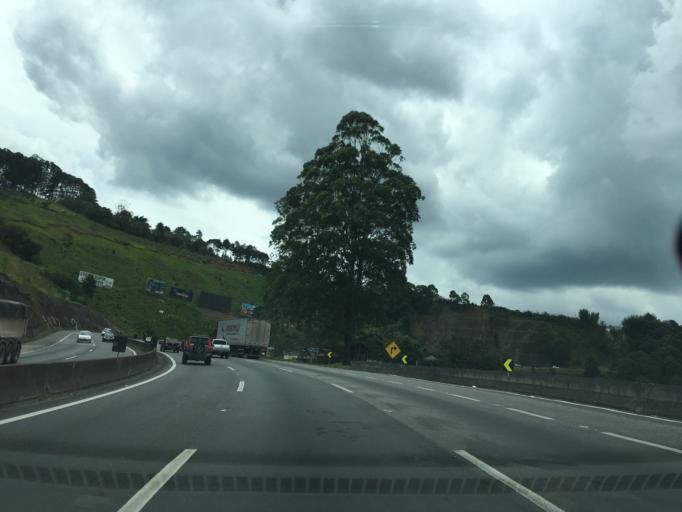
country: BR
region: Sao Paulo
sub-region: Mairipora
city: Mairipora
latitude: -23.2892
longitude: -46.5836
